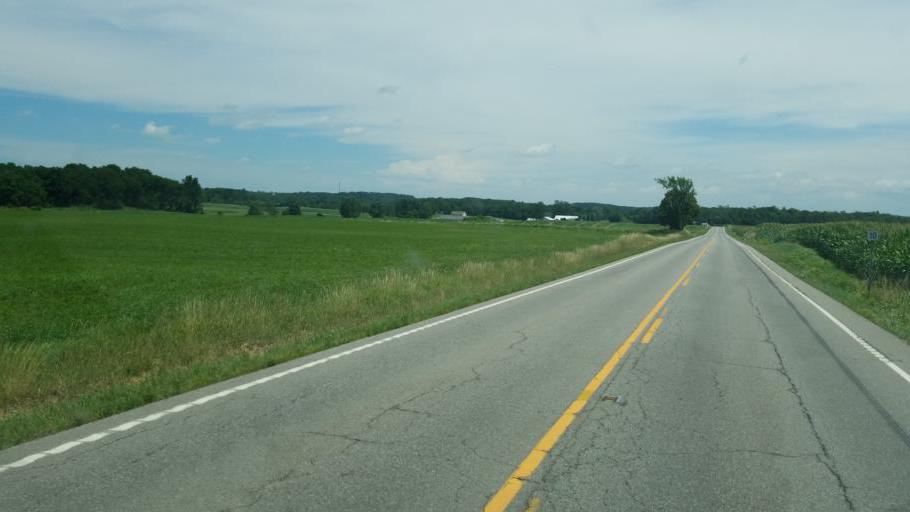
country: US
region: Ohio
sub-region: Richland County
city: Shelby
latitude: 40.8946
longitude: -82.5413
